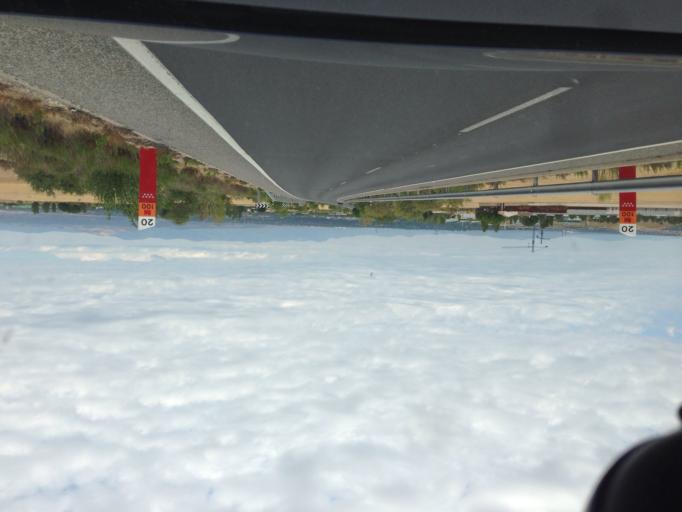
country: ES
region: Madrid
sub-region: Provincia de Madrid
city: Cobena
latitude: 40.5751
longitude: -3.5333
